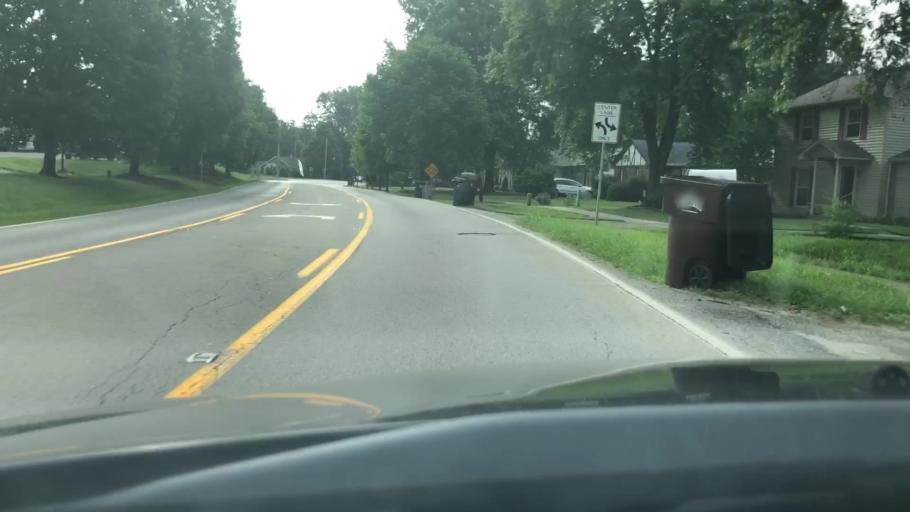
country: US
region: Kentucky
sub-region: Jefferson County
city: Graymoor-Devondale
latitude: 38.2659
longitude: -85.6117
